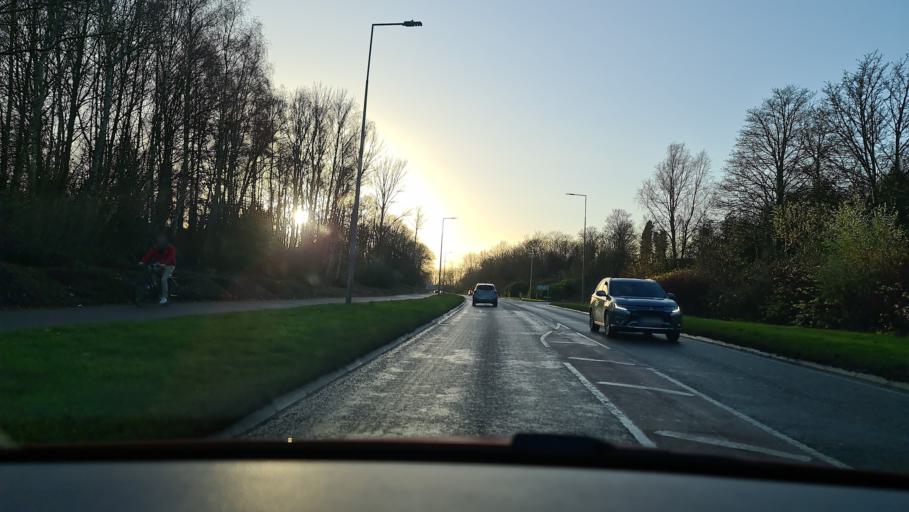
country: GB
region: England
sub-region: Milton Keynes
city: Loughton
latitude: 52.0367
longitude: -0.7993
